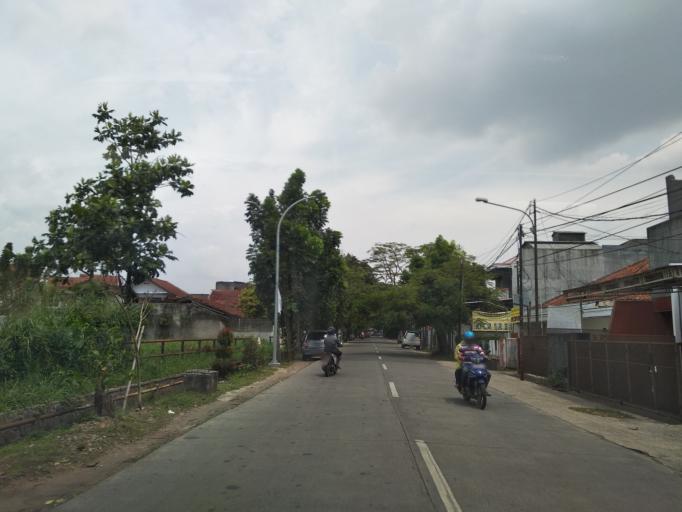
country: ID
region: West Java
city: Bandung
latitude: -6.9454
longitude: 107.6343
